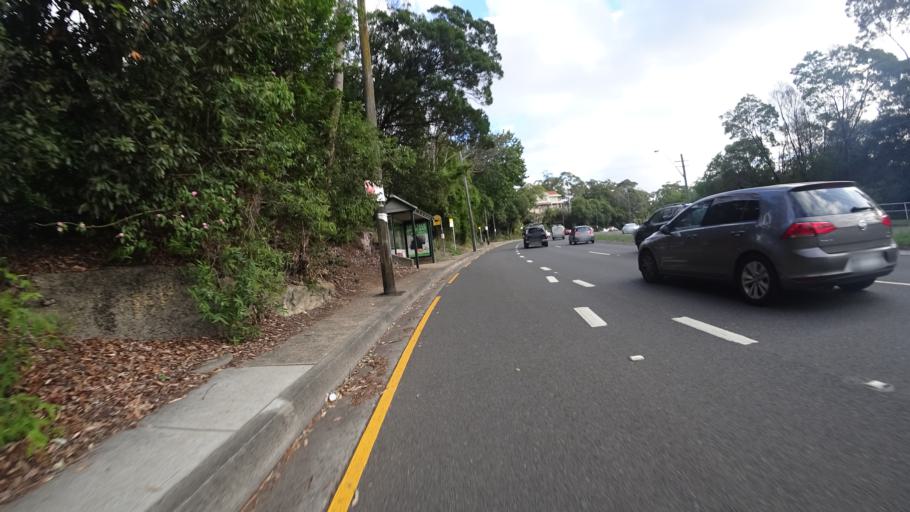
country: AU
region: New South Wales
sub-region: Lane Cove
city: Lane Cove West
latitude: -33.8256
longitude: 151.1501
